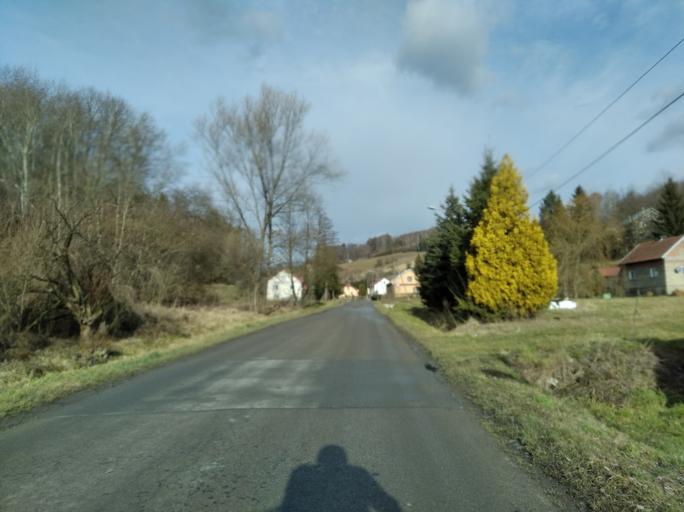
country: PL
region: Subcarpathian Voivodeship
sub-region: Powiat strzyzowski
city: Strzyzow
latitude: 49.8922
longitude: 21.7552
